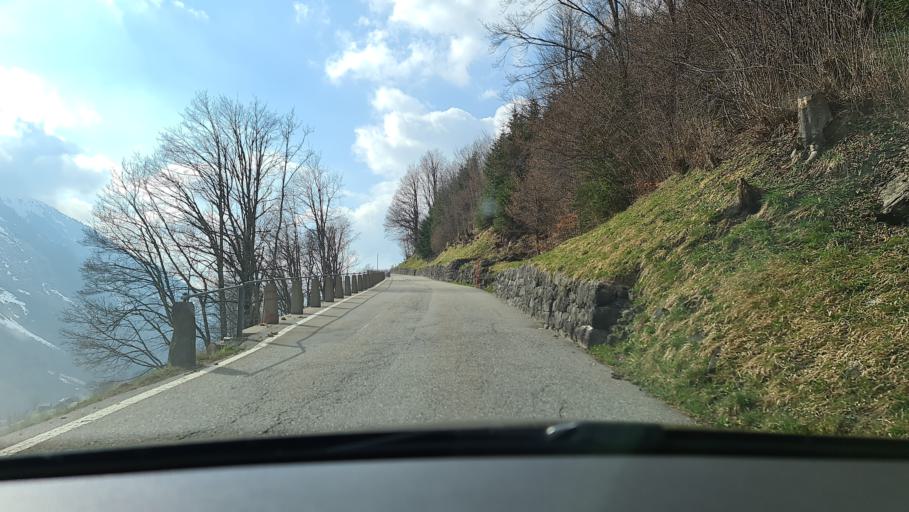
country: CH
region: Uri
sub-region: Uri
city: Burglen
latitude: 46.8669
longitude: 8.7726
